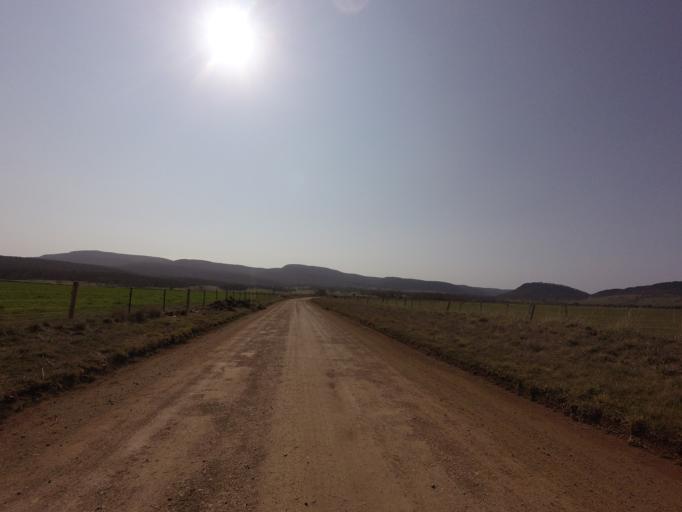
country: AU
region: Tasmania
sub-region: Break O'Day
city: St Helens
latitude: -41.8210
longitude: 147.9352
